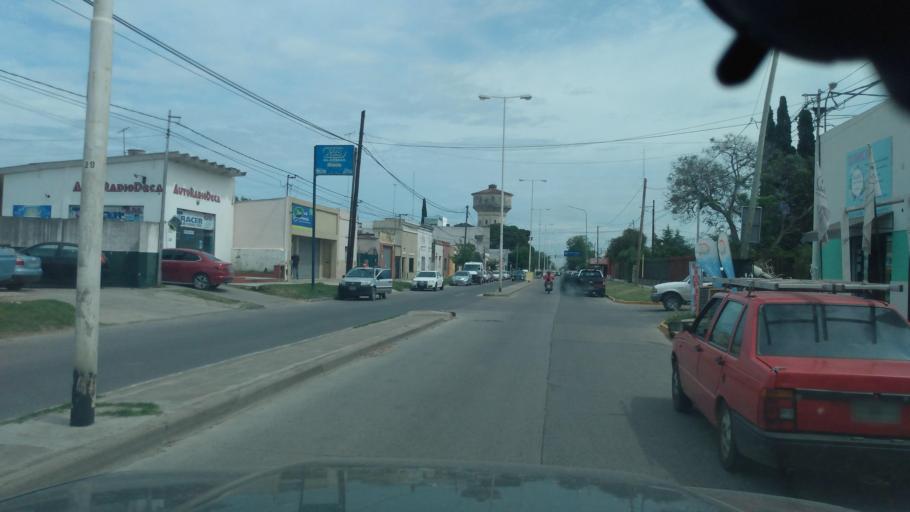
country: AR
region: Buenos Aires
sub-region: Partido de Lujan
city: Lujan
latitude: -34.5740
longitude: -59.0912
